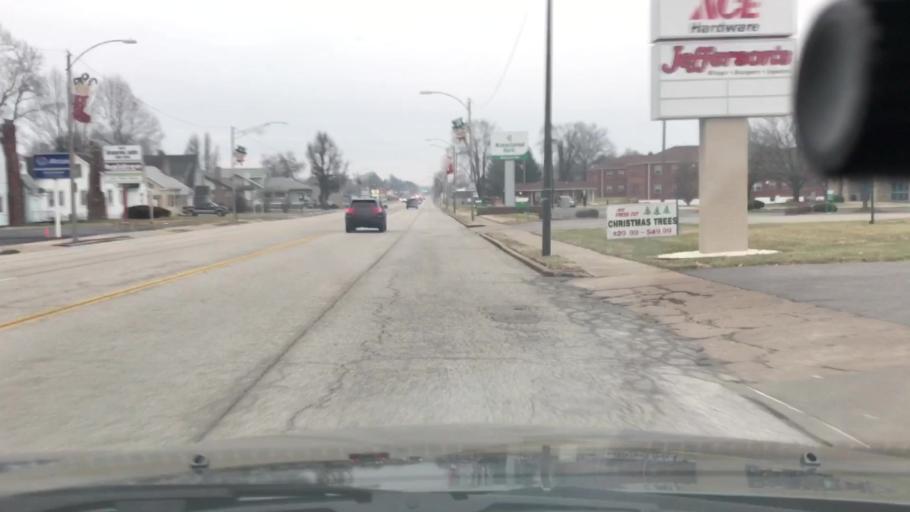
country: US
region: Illinois
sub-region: Saint Clair County
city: Swansea
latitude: 38.5566
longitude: -90.0430
